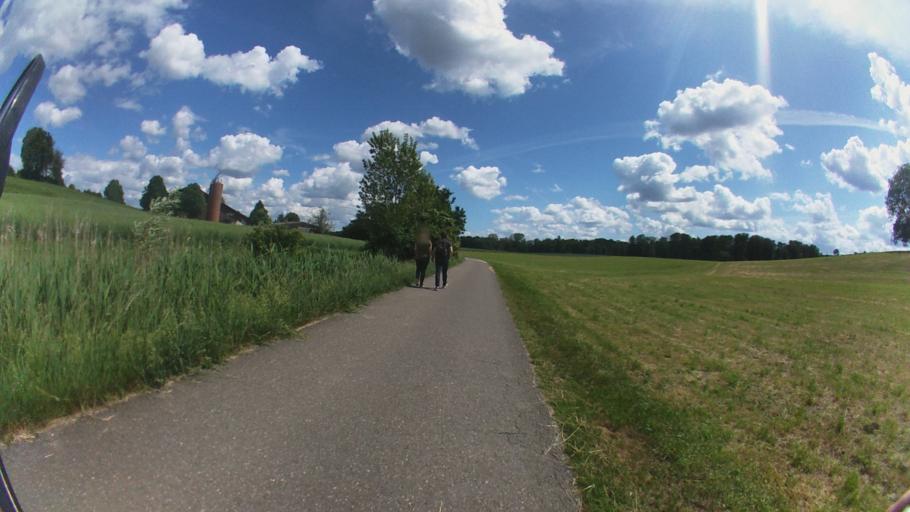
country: CH
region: Zurich
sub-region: Bezirk Dielsdorf
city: Regensdorf
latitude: 47.4396
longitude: 8.4867
